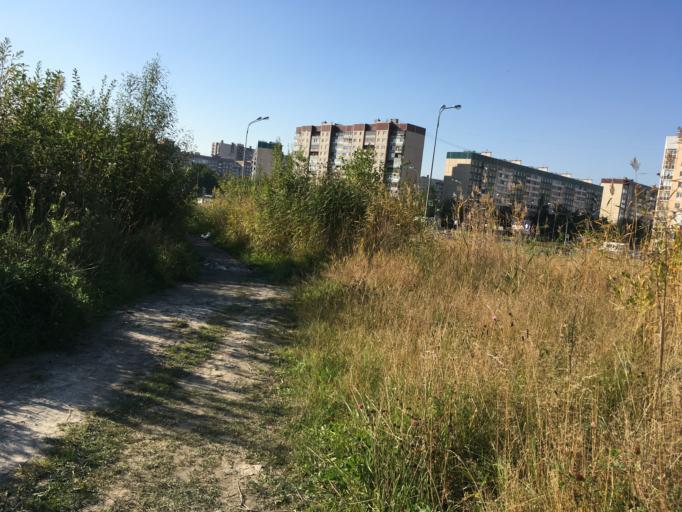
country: RU
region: St.-Petersburg
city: Komendantsky aerodrom
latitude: 60.0189
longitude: 30.2588
